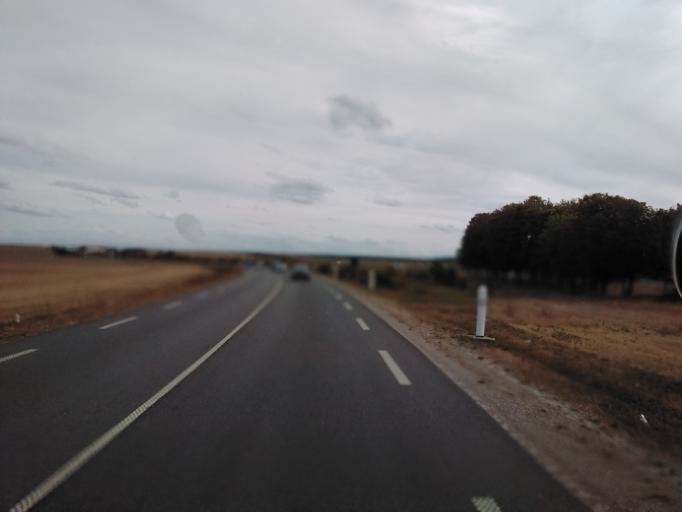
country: FR
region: Champagne-Ardenne
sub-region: Departement de la Marne
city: Verzenay
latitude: 49.1754
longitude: 4.1663
